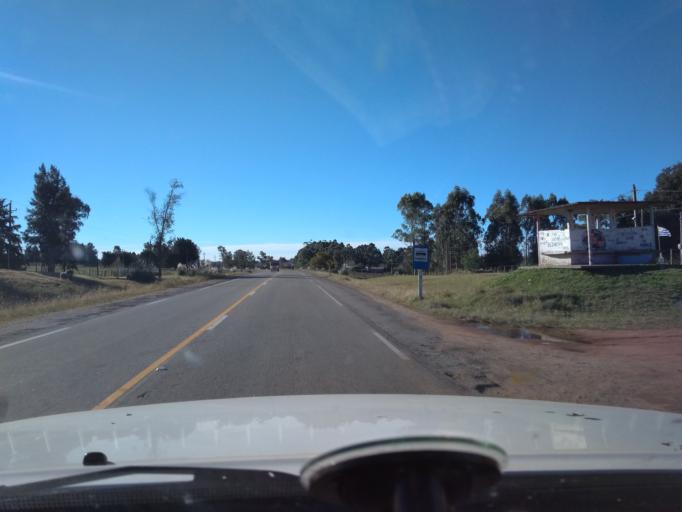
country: UY
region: Canelones
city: Sauce
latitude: -34.6111
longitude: -56.0485
